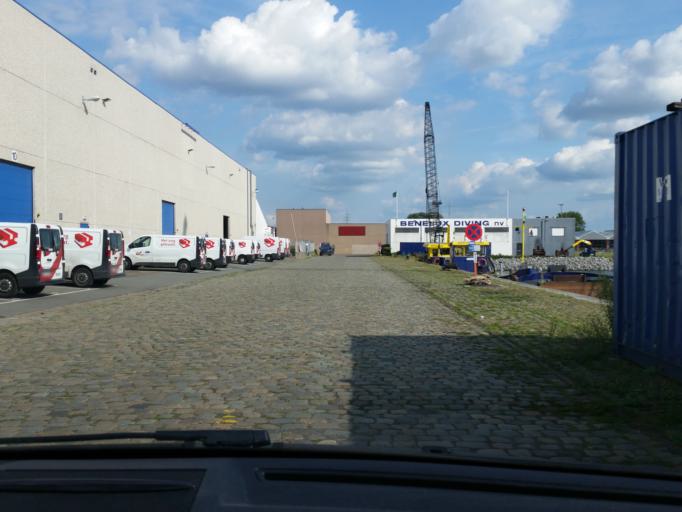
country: BE
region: Flanders
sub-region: Provincie Antwerpen
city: Antwerpen
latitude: 51.2375
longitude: 4.4153
